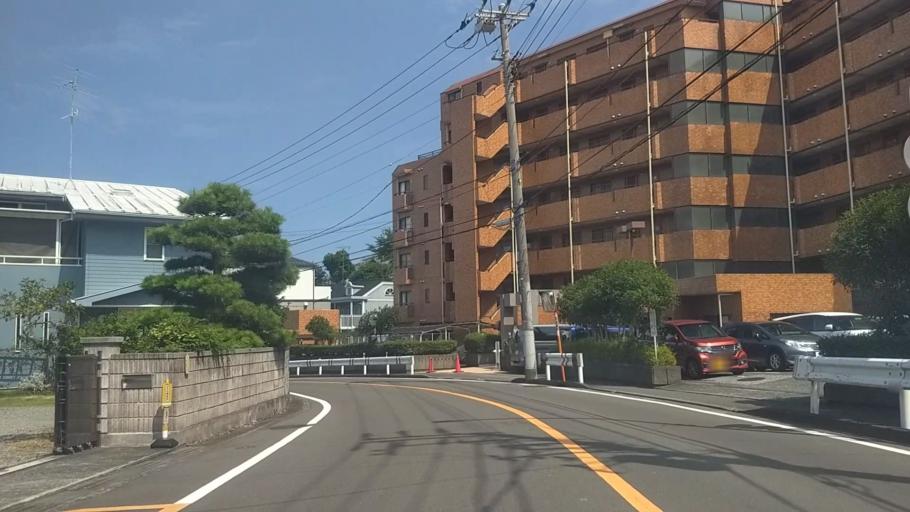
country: JP
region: Kanagawa
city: Yokohama
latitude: 35.4925
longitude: 139.5933
